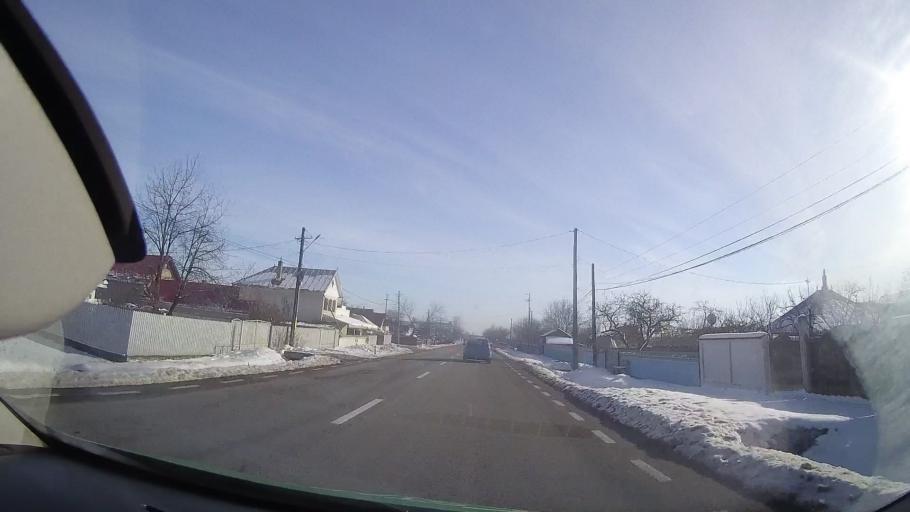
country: RO
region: Neamt
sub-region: Comuna Negresti
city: Negresti
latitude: 47.0567
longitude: 26.3926
